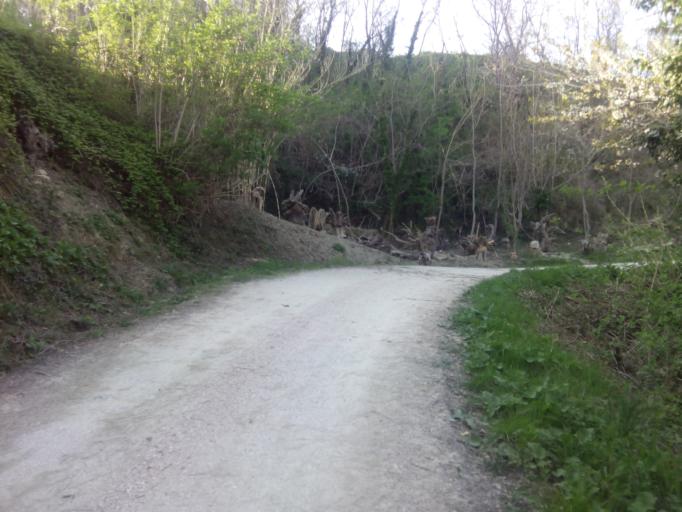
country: IT
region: Emilia-Romagna
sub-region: Provincia di Rimini
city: Mondaino
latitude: 43.8539
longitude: 12.6562
